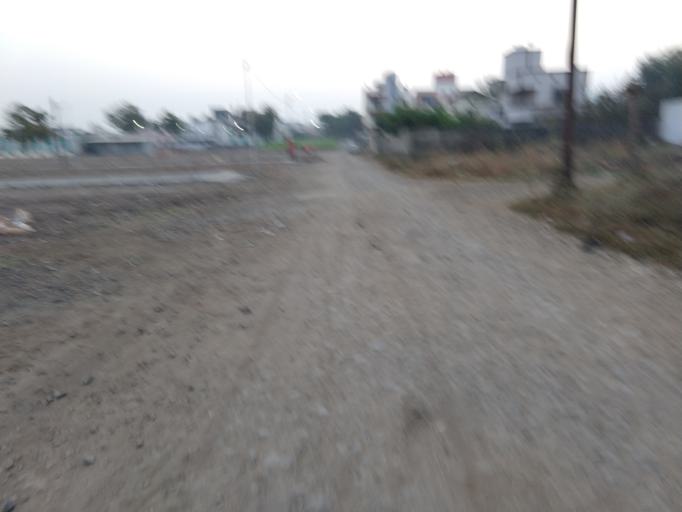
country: IN
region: Maharashtra
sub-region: Pune Division
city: Pune
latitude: 18.4387
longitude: 73.9120
